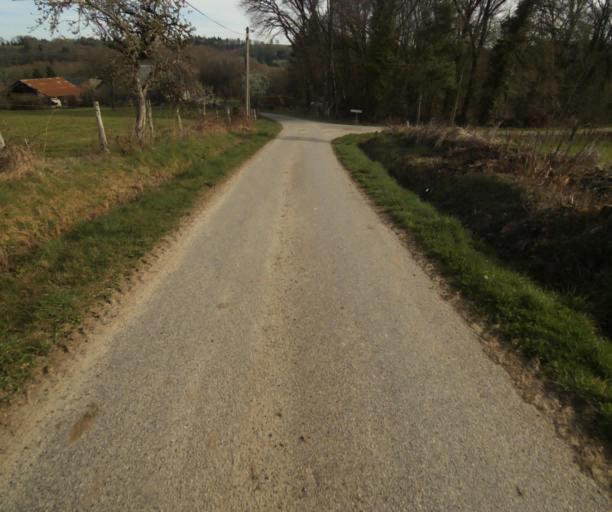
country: FR
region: Limousin
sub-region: Departement de la Correze
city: Chamboulive
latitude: 45.4409
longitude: 1.7451
